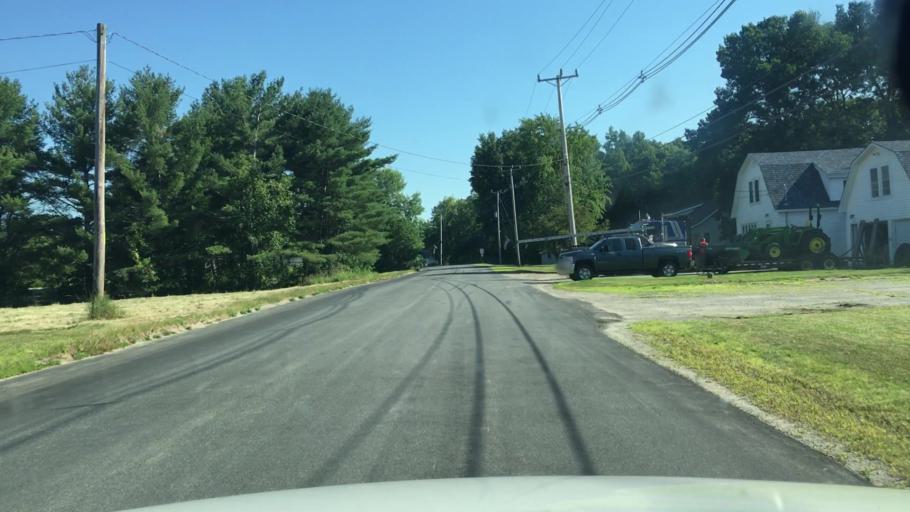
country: US
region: Maine
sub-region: Penobscot County
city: Howland
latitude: 45.2329
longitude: -68.6491
